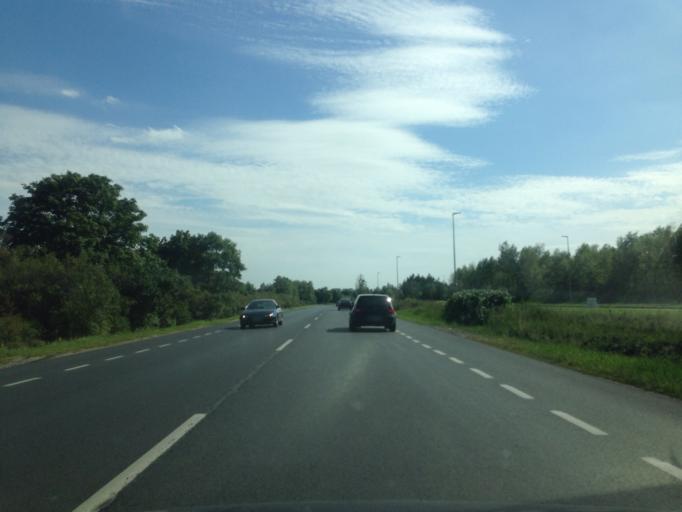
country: PL
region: Kujawsko-Pomorskie
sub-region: Torun
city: Torun
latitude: 53.0472
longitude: 18.6164
